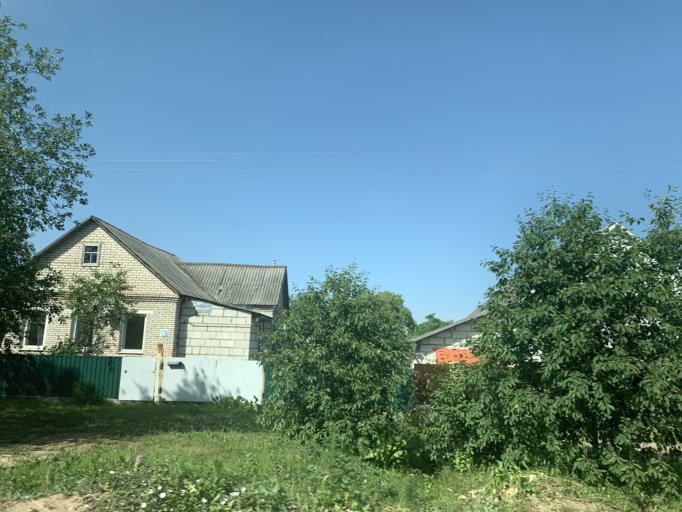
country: BY
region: Minsk
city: Dzyarzhynsk
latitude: 53.6990
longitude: 27.1017
